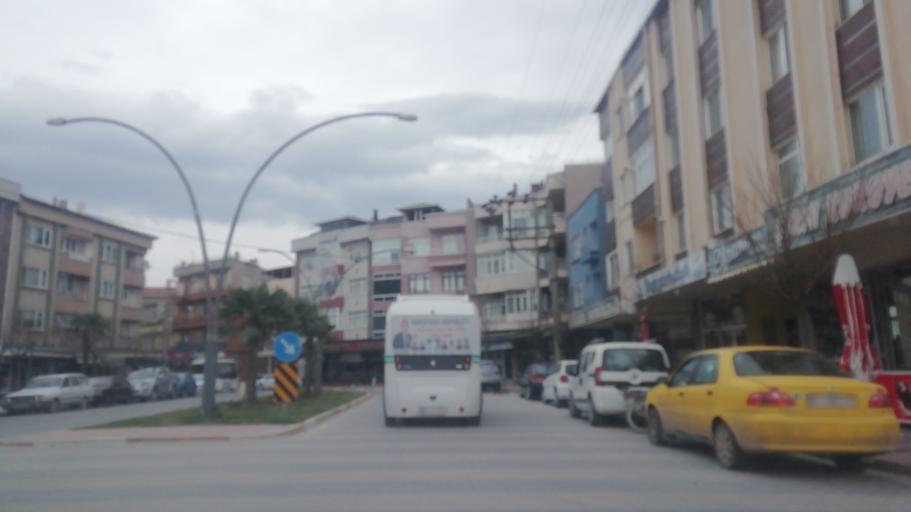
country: TR
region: Balikesir
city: Gonen
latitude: 40.1020
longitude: 27.6521
